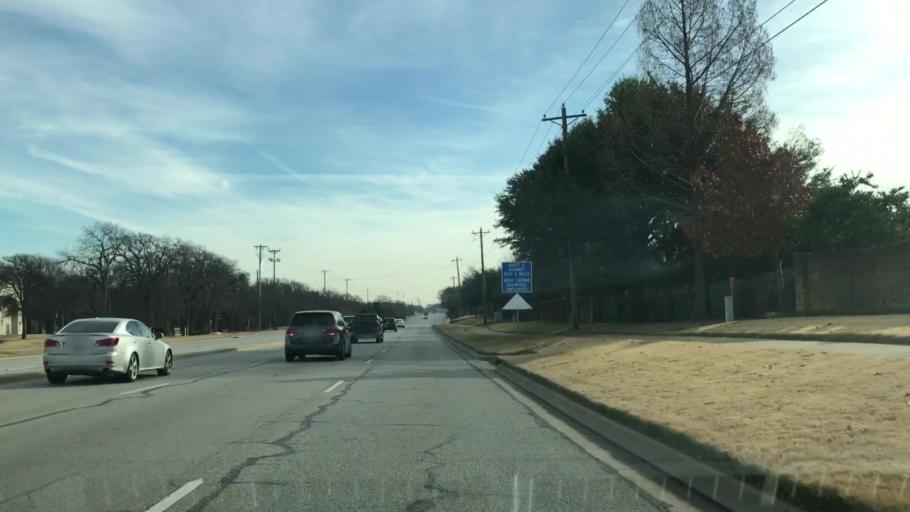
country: US
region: Texas
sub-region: Tarrant County
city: Southlake
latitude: 32.9413
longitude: -97.1711
